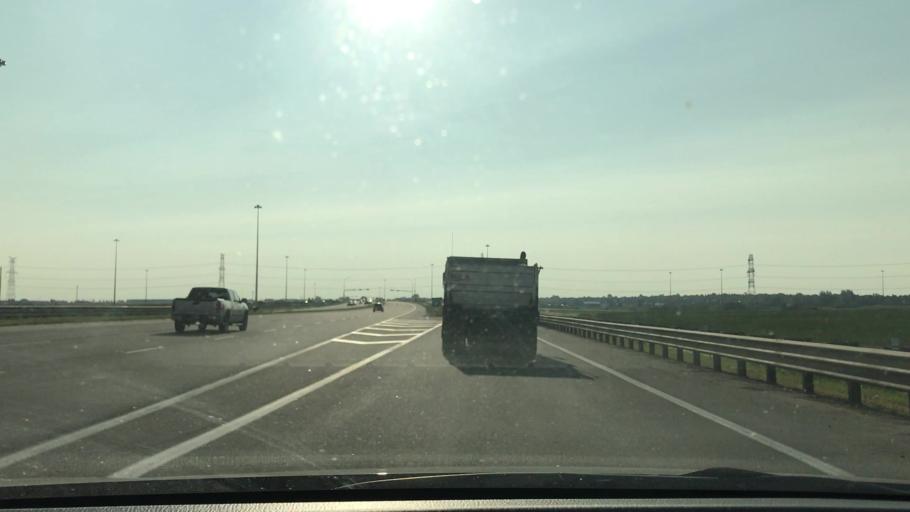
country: CA
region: Alberta
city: Sherwood Park
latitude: 53.5402
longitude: -113.3507
